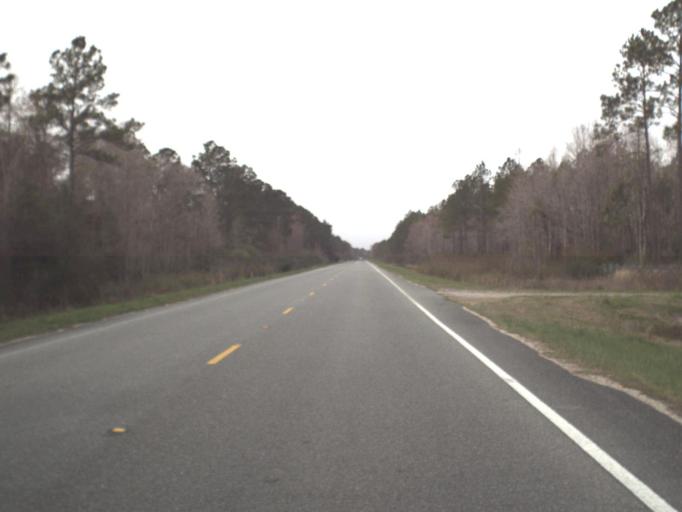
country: US
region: Florida
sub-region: Leon County
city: Woodville
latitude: 30.1923
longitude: -84.0967
